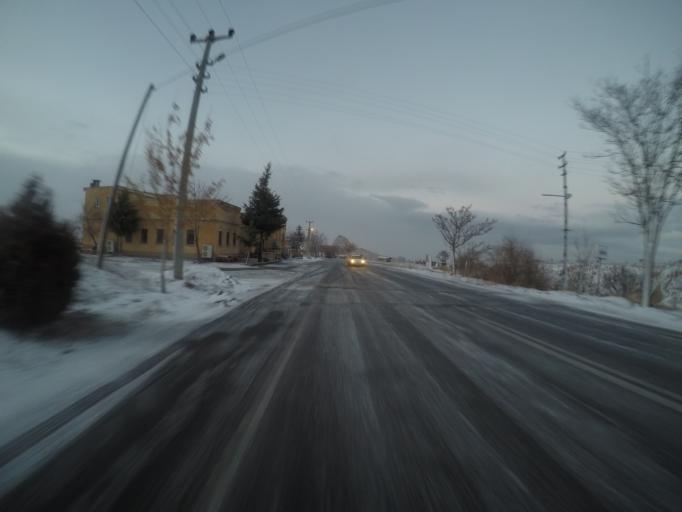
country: TR
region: Nevsehir
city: Goereme
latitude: 38.6189
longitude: 34.8045
